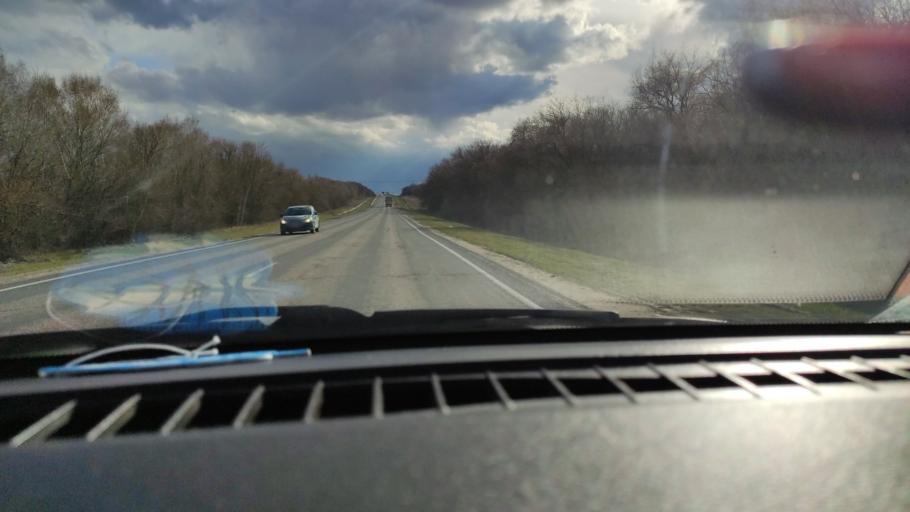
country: RU
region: Saratov
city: Sinodskoye
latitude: 51.9636
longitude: 46.6288
